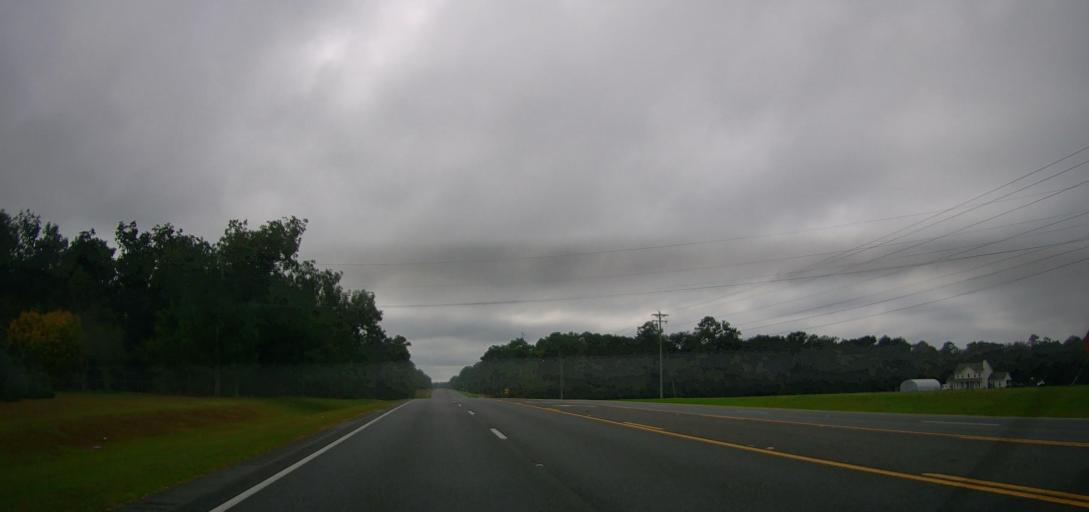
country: US
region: Georgia
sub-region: Thomas County
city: Thomasville
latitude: 30.9144
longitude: -83.9191
